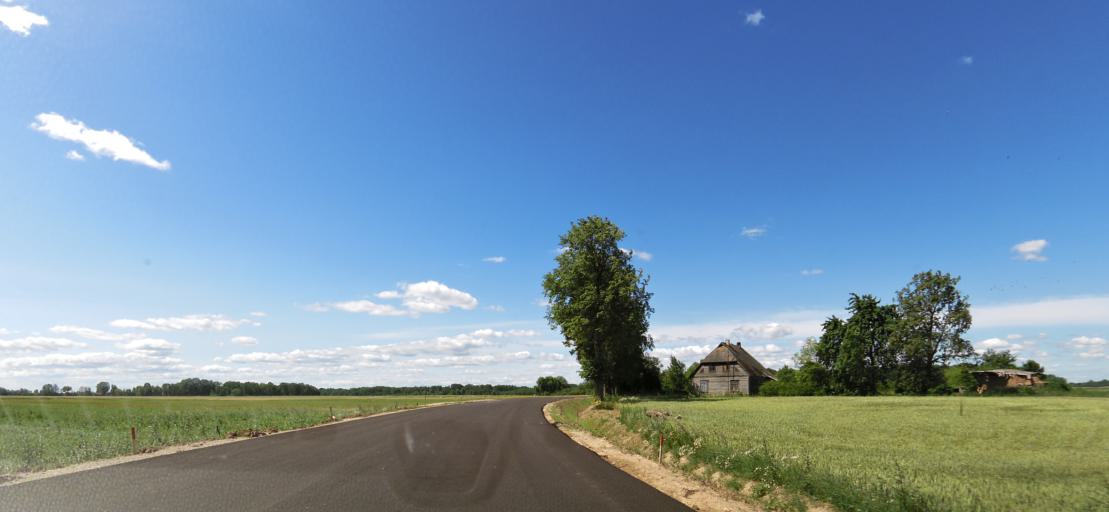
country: LT
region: Panevezys
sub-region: Birzai
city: Birzai
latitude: 56.2986
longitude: 24.6132
